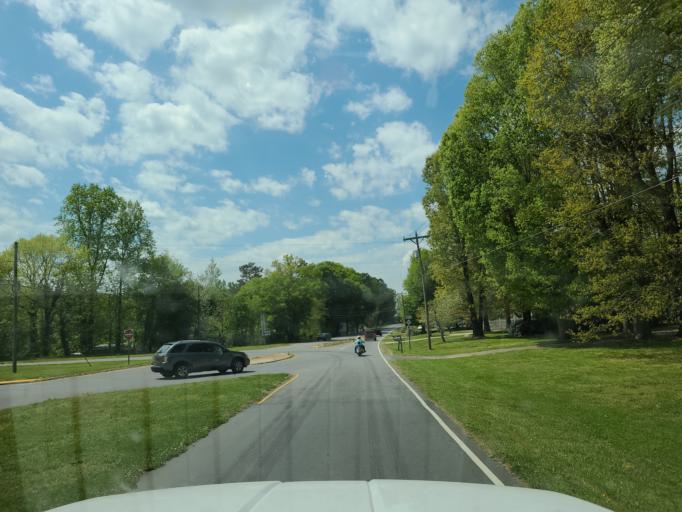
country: US
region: North Carolina
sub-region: Lincoln County
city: Lincolnton
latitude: 35.4391
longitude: -81.2820
